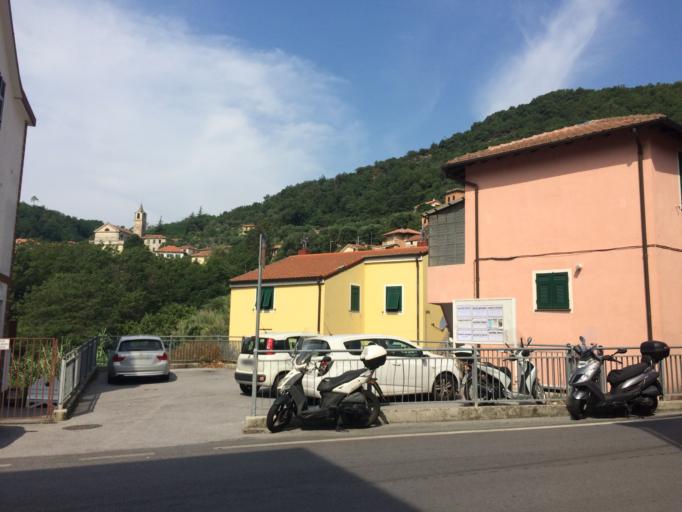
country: IT
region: Liguria
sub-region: Provincia di Savona
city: Celle Ligure
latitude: 44.3875
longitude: 8.5494
